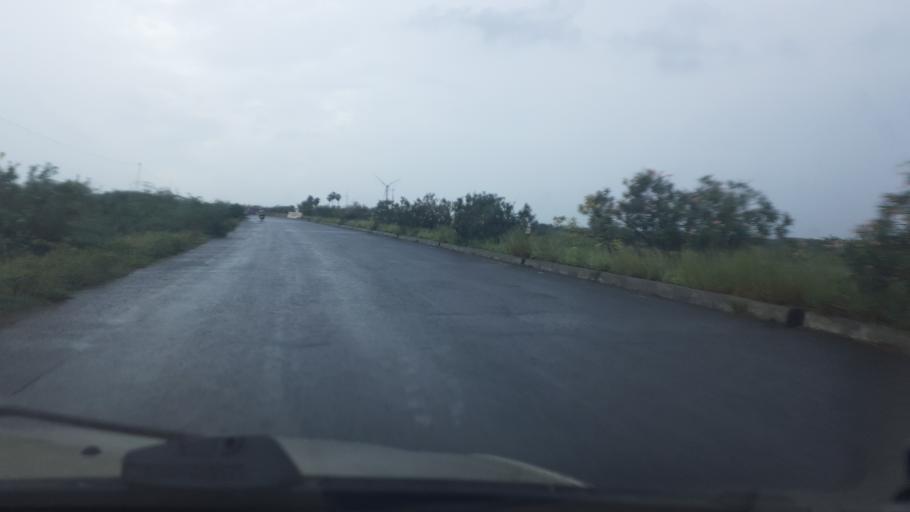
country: IN
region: Tamil Nadu
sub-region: Thoothukkudi
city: Kayattar
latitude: 9.0090
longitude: 77.7825
